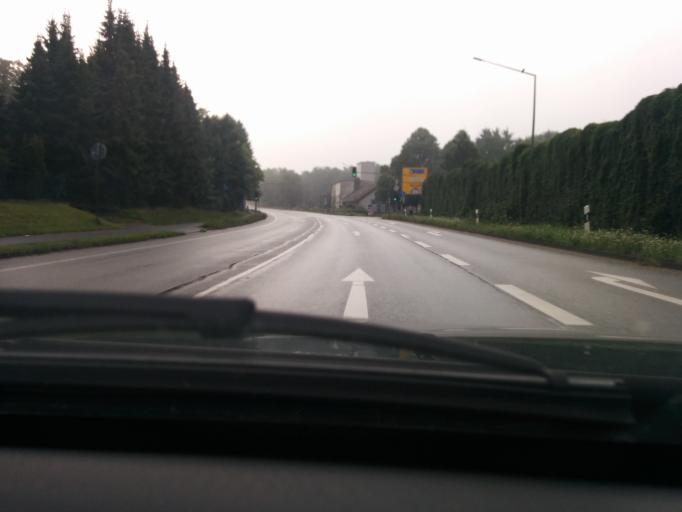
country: DE
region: North Rhine-Westphalia
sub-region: Regierungsbezirk Detmold
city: Steinhagen
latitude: 52.0230
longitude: 8.4223
